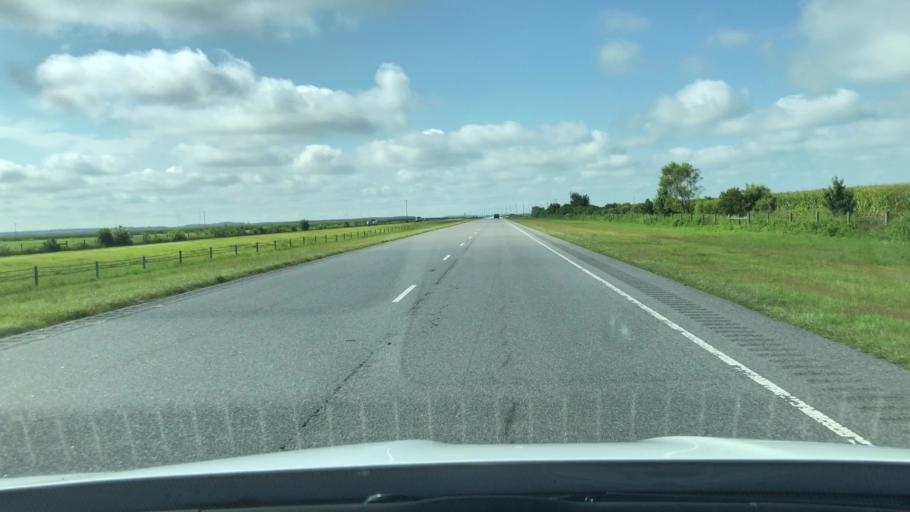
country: US
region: North Carolina
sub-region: Pasquotank County
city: Elizabeth City
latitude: 36.3454
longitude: -76.3137
